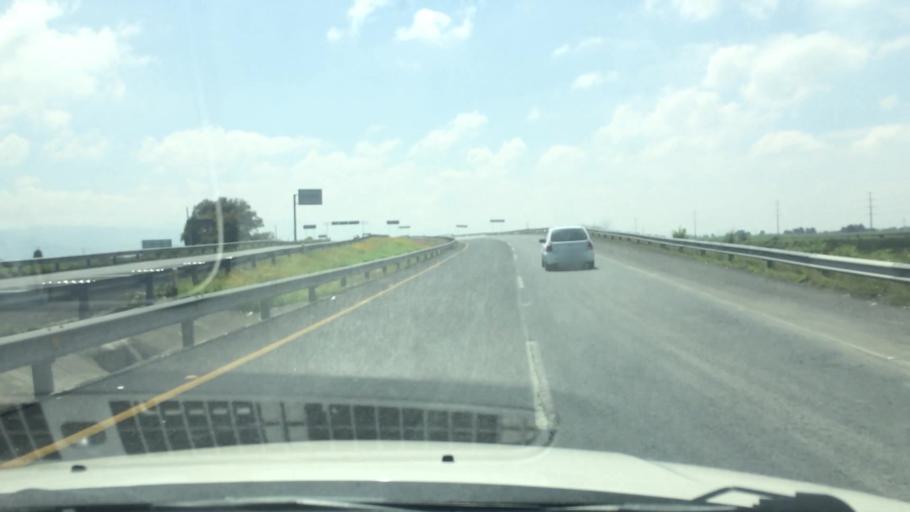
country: MX
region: Mexico
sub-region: Toluca
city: La Constitucion Toltepec
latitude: 19.3743
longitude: -99.5481
